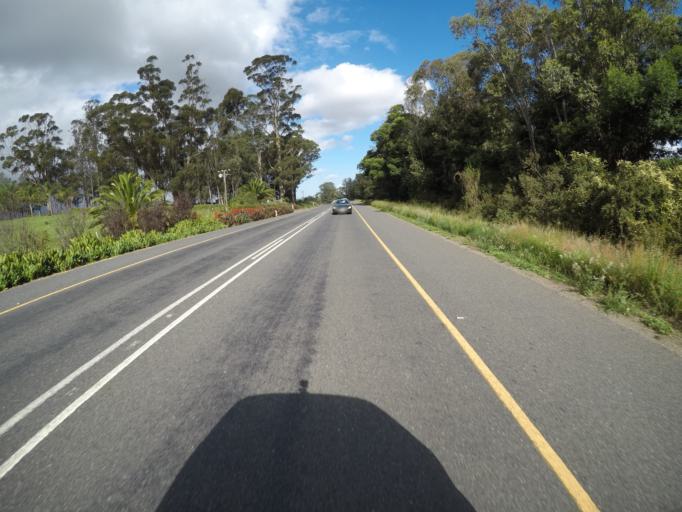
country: ZA
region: Western Cape
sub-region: Overberg District Municipality
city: Swellendam
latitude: -34.0121
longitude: 20.3924
